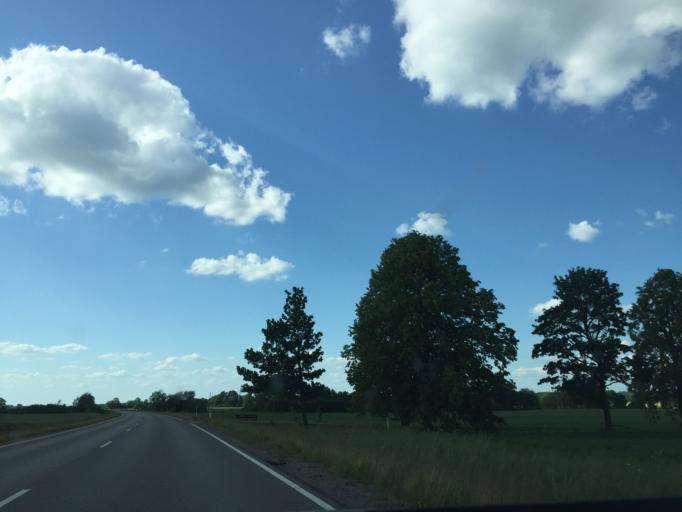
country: LV
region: Kandava
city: Kandava
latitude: 56.9036
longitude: 22.8467
